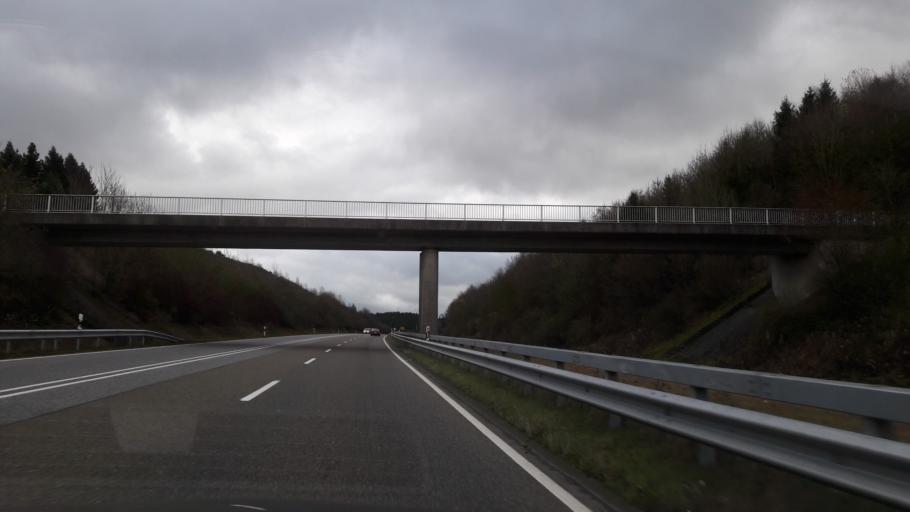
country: DE
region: Rheinland-Pfalz
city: Winterspelt
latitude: 50.2200
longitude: 6.2263
